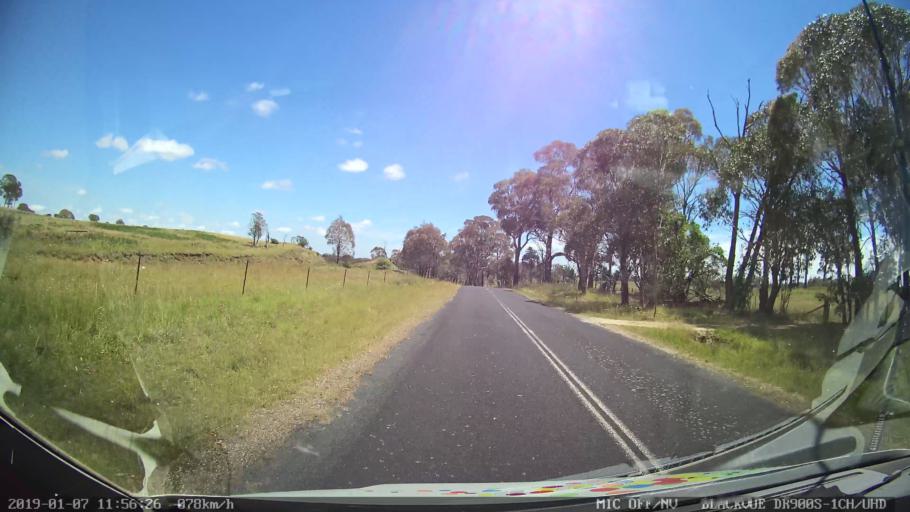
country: AU
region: New South Wales
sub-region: Guyra
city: Guyra
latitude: -30.2746
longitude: 151.6737
